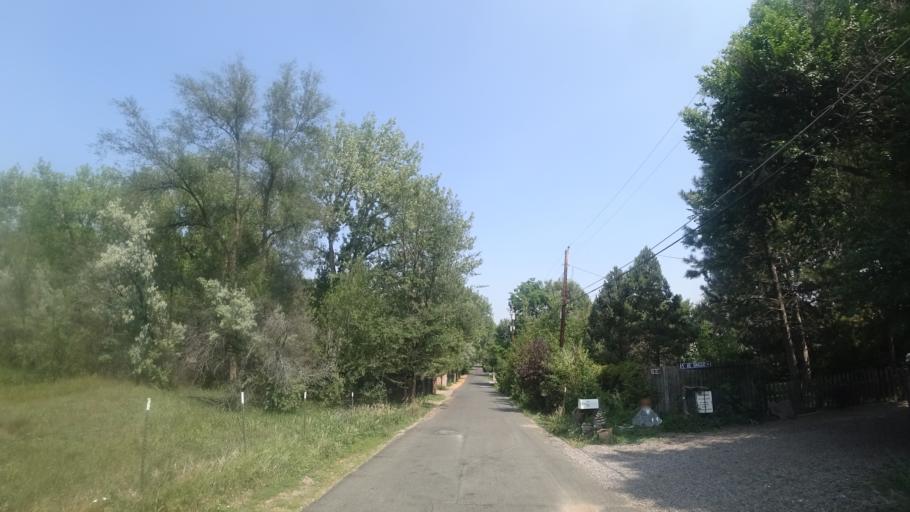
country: US
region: Colorado
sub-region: Arapahoe County
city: Cherry Hills Village
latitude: 39.6351
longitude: -104.9679
